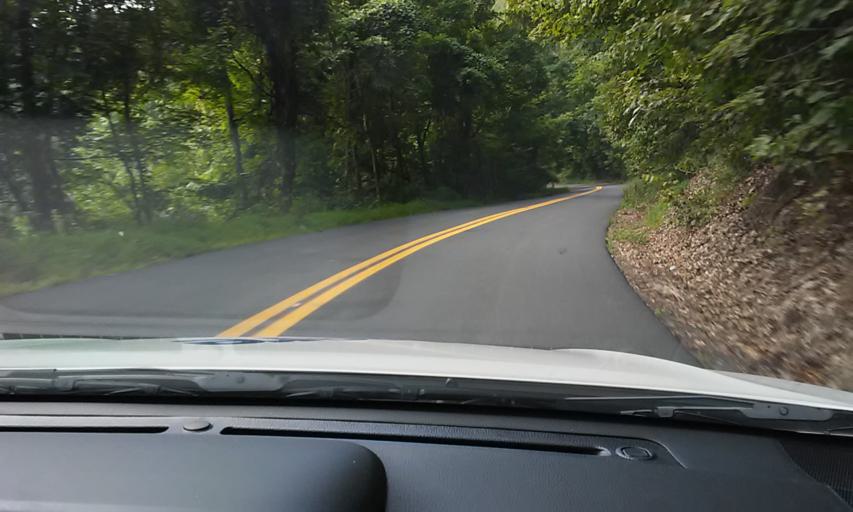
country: US
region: West Virginia
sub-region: Marion County
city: Mannington
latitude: 39.6328
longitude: -80.2883
